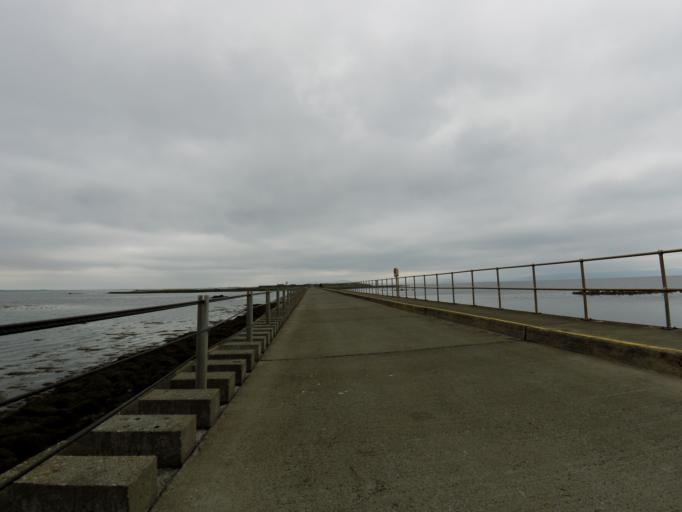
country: IE
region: Connaught
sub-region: County Galway
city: Gaillimh
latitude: 53.2600
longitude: -9.0562
